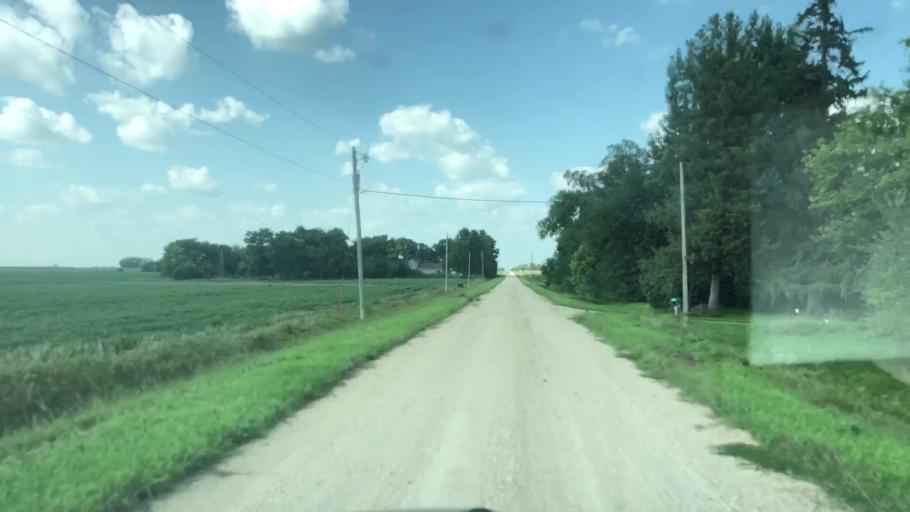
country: US
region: Iowa
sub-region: O'Brien County
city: Sheldon
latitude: 43.1722
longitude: -95.7823
